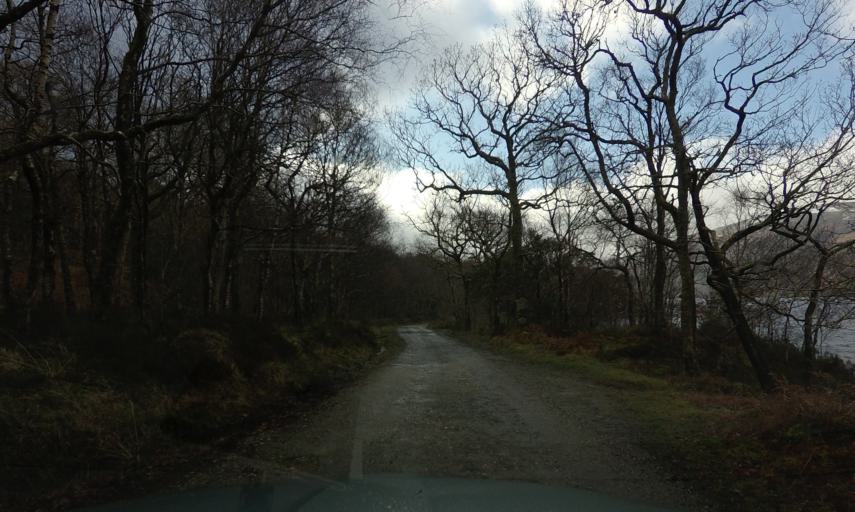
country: GB
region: Scotland
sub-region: West Dunbartonshire
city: Balloch
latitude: 56.1548
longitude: -4.6425
